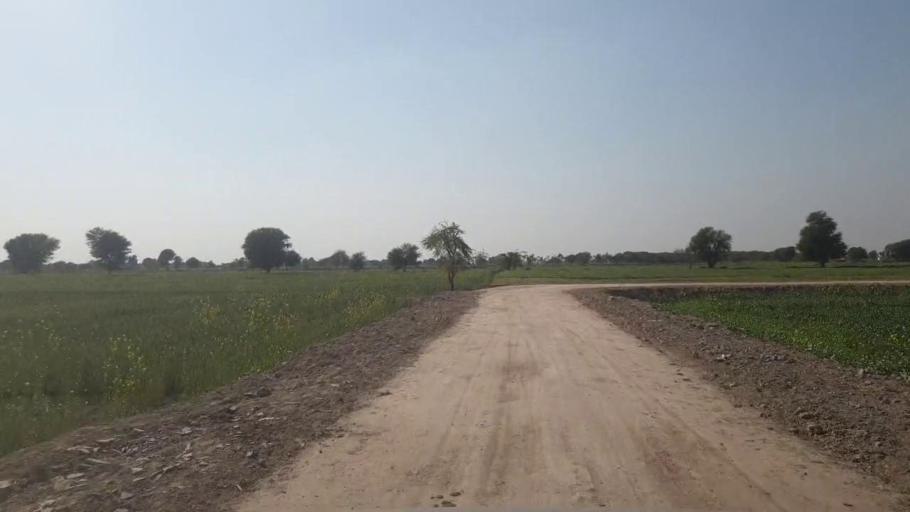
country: PK
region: Sindh
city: Chambar
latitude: 25.3232
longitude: 68.8532
